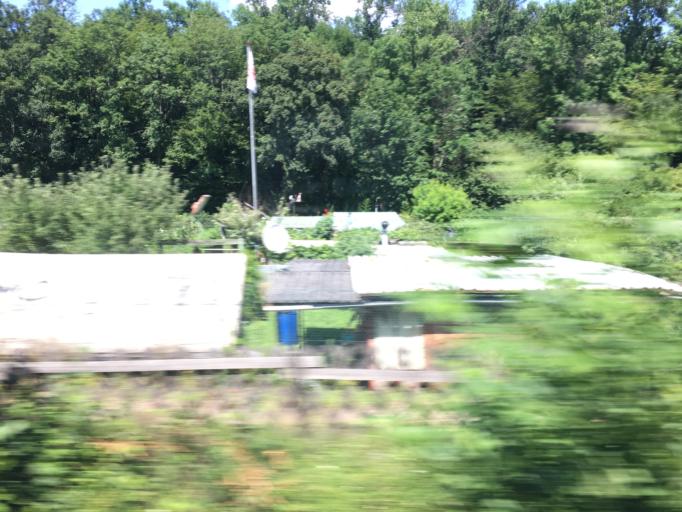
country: DE
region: Hesse
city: Niederrad
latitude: 50.1156
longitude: 8.6135
